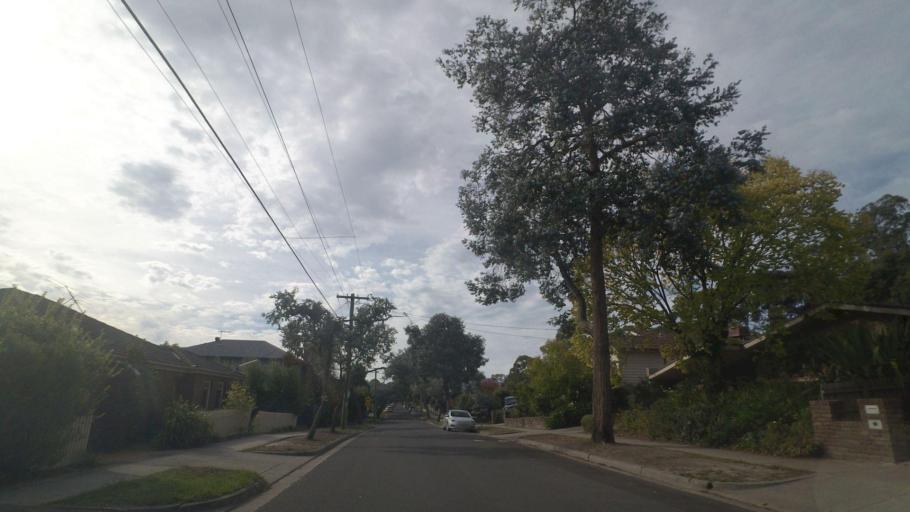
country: AU
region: Victoria
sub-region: Whitehorse
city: Blackburn
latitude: -37.8248
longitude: 145.1414
